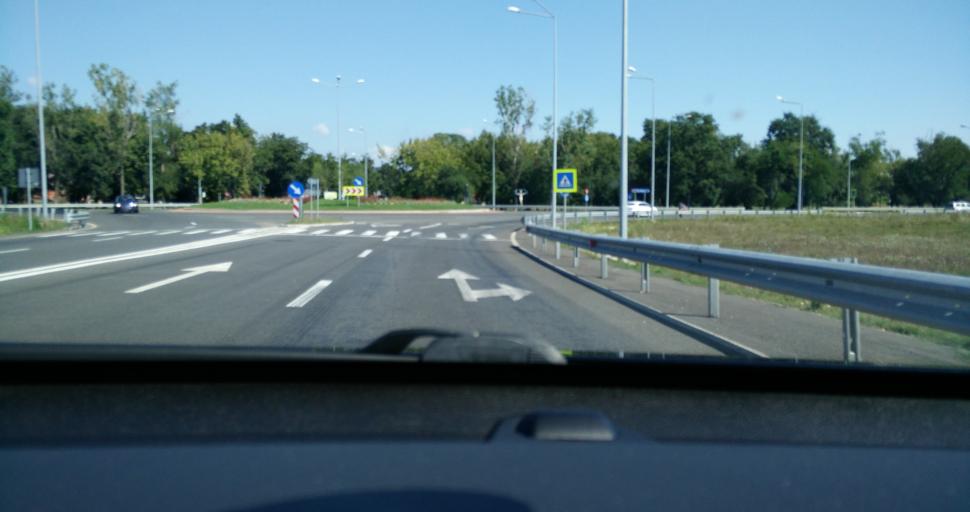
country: RO
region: Bihor
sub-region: Comuna Sanmartin
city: Sanmartin
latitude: 47.0359
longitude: 21.9963
